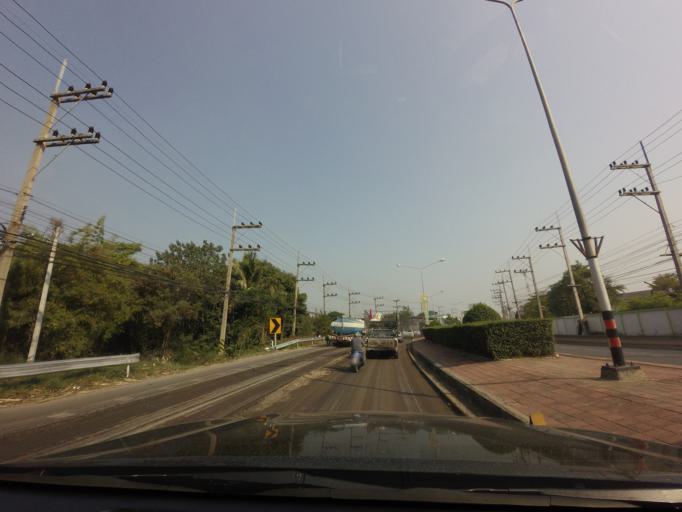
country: TH
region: Kanchanaburi
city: Tha Maka
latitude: 13.8979
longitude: 99.7939
